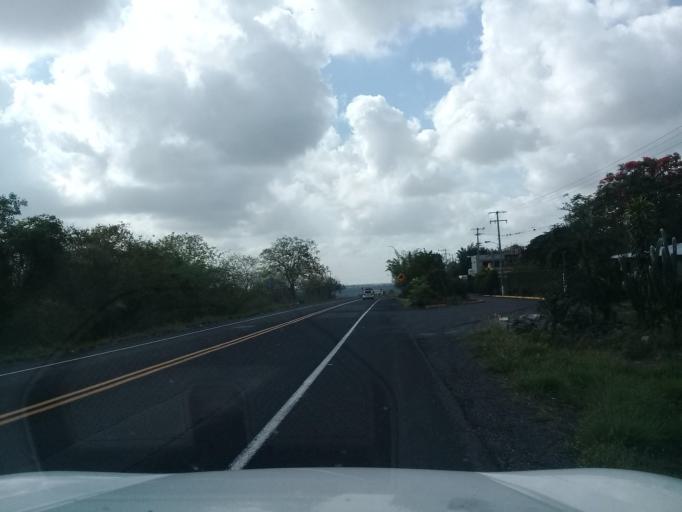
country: MX
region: Veracruz
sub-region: Emiliano Zapata
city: Plan del Rio
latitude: 19.4108
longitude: -96.6501
